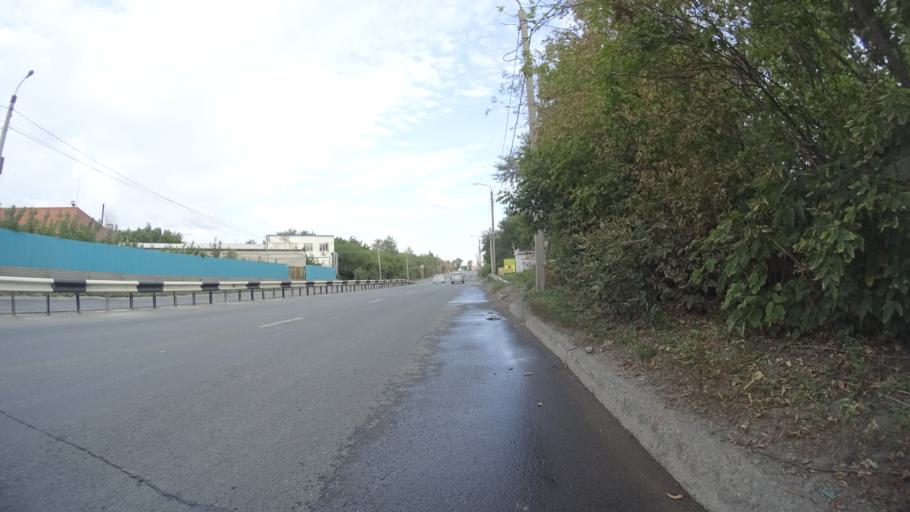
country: RU
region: Chelyabinsk
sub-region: Gorod Chelyabinsk
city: Chelyabinsk
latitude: 55.1936
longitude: 61.4180
